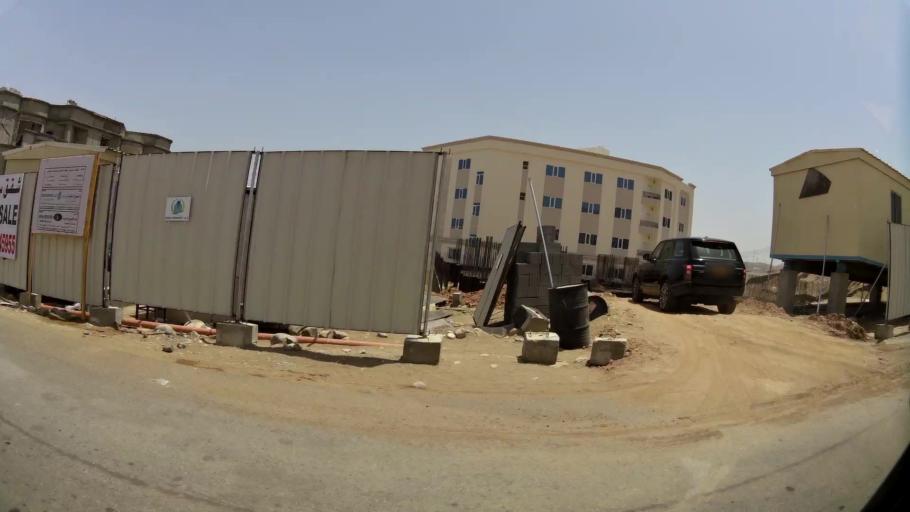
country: OM
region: Muhafazat Masqat
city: Bawshar
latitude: 23.5753
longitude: 58.4262
